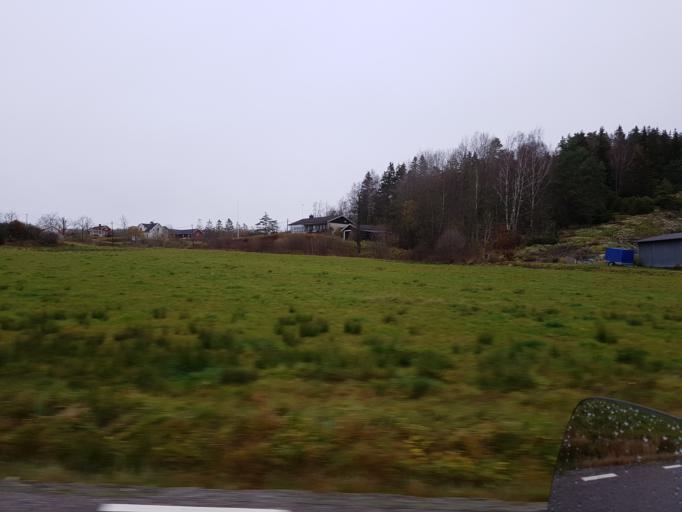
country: SE
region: Vaestra Goetaland
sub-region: Orust
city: Henan
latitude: 58.2568
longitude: 11.7434
